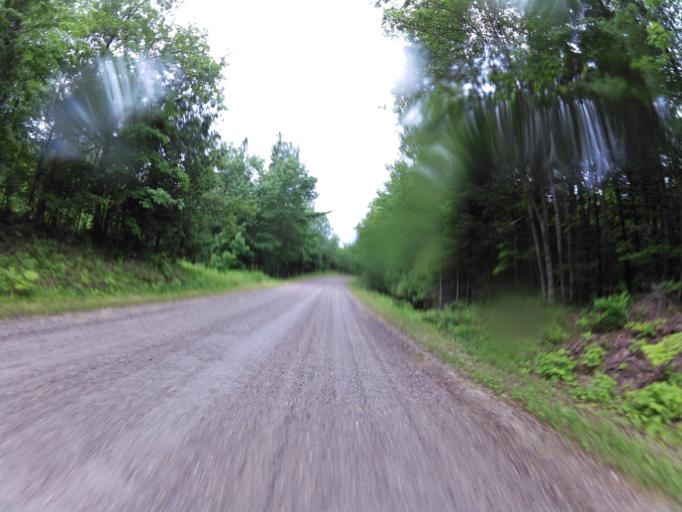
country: CA
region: Ontario
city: Renfrew
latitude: 45.0919
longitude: -76.5929
